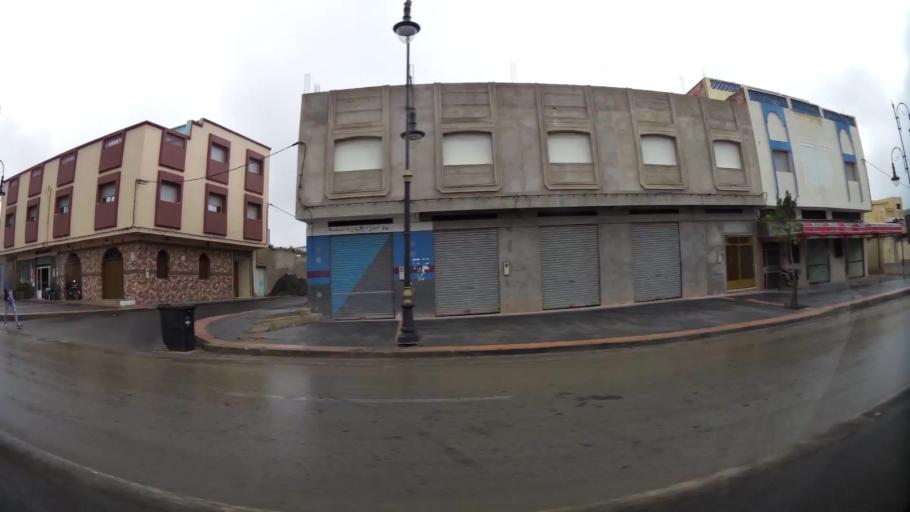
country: MA
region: Taza-Al Hoceima-Taounate
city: Imzourene
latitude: 35.1745
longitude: -3.8673
